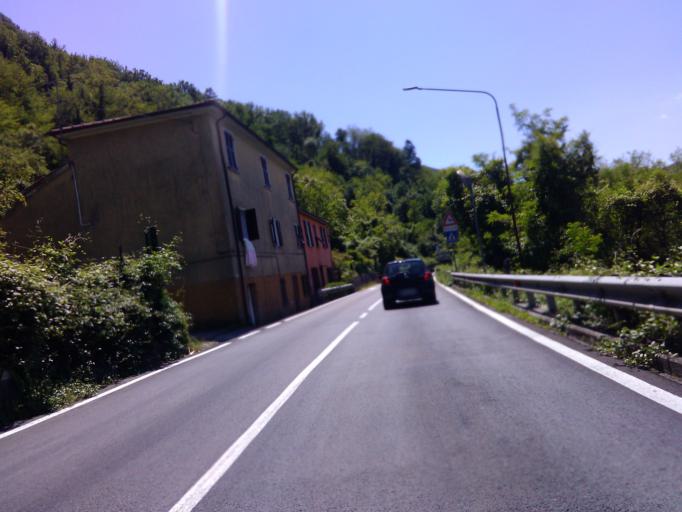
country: IT
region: Tuscany
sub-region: Provincia di Massa-Carrara
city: Aulla
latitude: 44.2014
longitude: 9.9629
